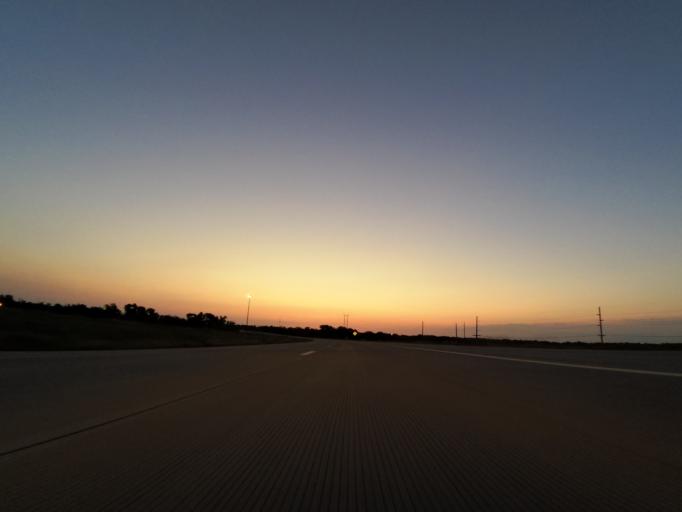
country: US
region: Kansas
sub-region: Reno County
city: South Hutchinson
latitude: 38.0129
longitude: -97.9203
